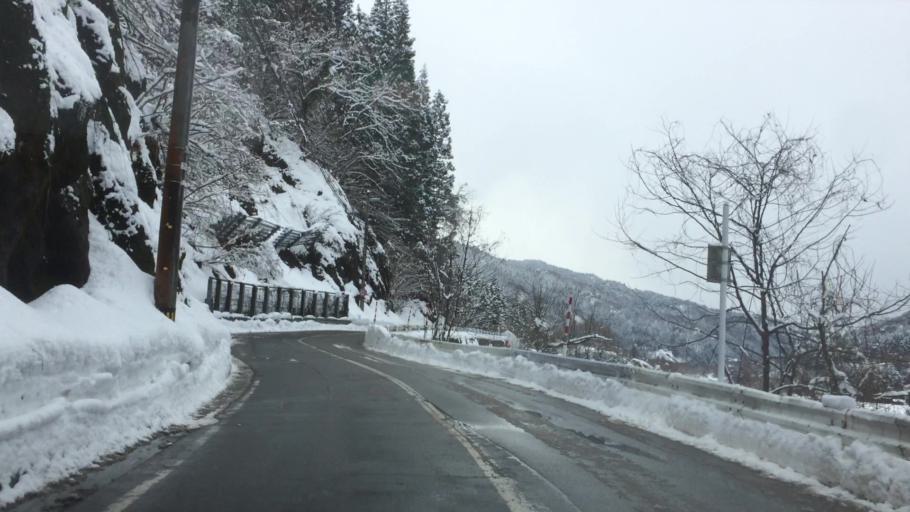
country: JP
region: Toyama
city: Kamiichi
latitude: 36.5715
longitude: 137.3702
